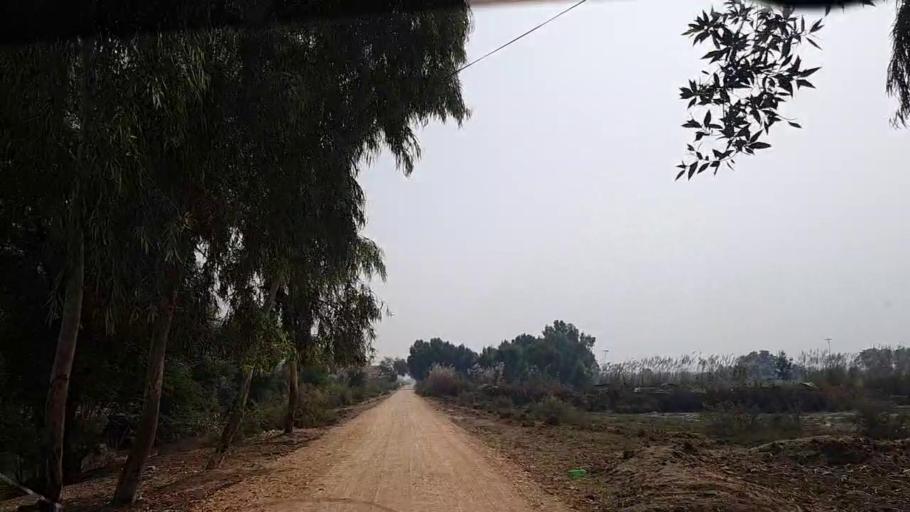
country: PK
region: Sindh
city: Garhi Yasin
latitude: 27.9313
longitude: 68.5567
